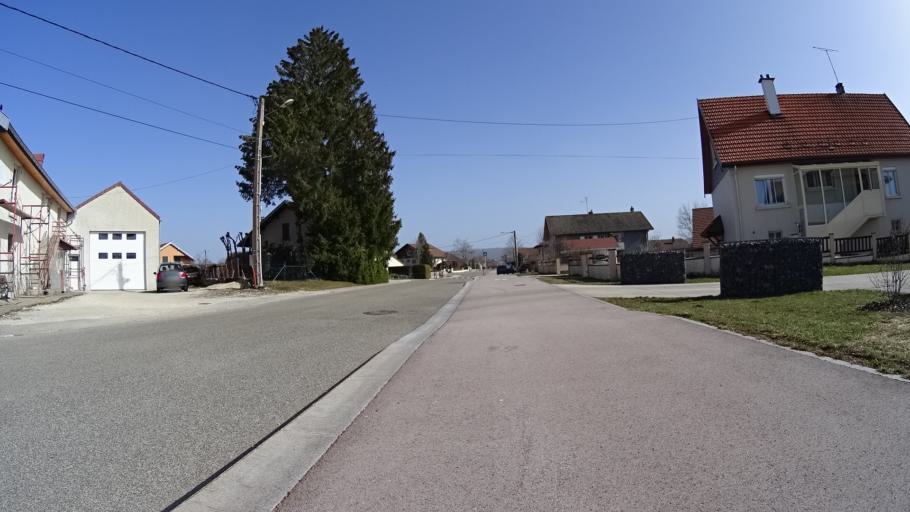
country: FR
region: Franche-Comte
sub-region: Departement du Doubs
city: Frasne
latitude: 46.8506
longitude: 6.1560
